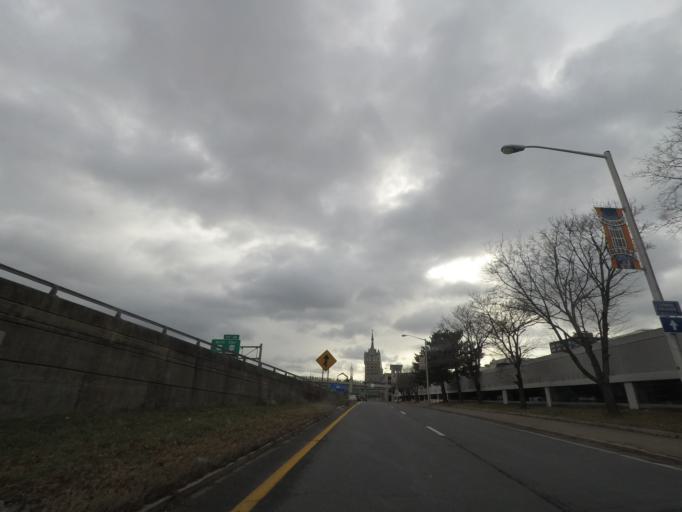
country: US
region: New York
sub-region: Albany County
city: Albany
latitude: 42.6517
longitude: -73.7480
